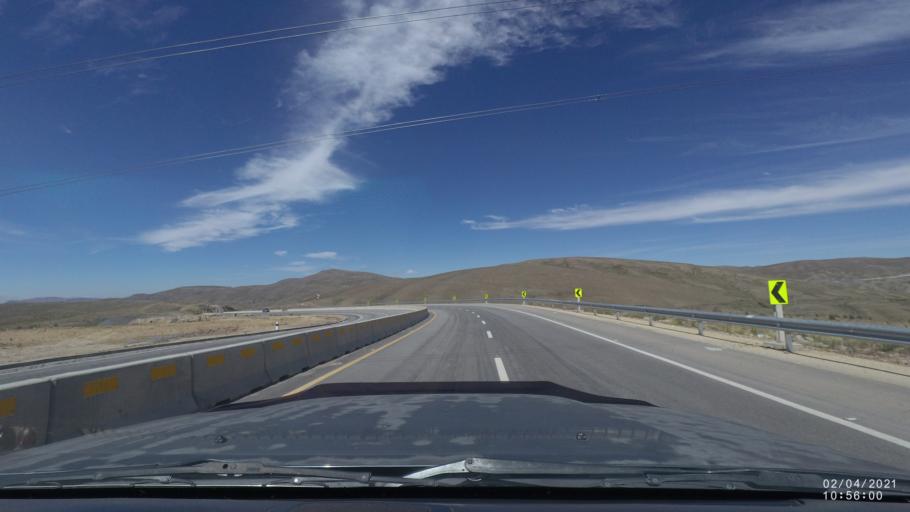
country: BO
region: Cochabamba
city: Colchani
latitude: -17.6831
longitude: -66.7538
